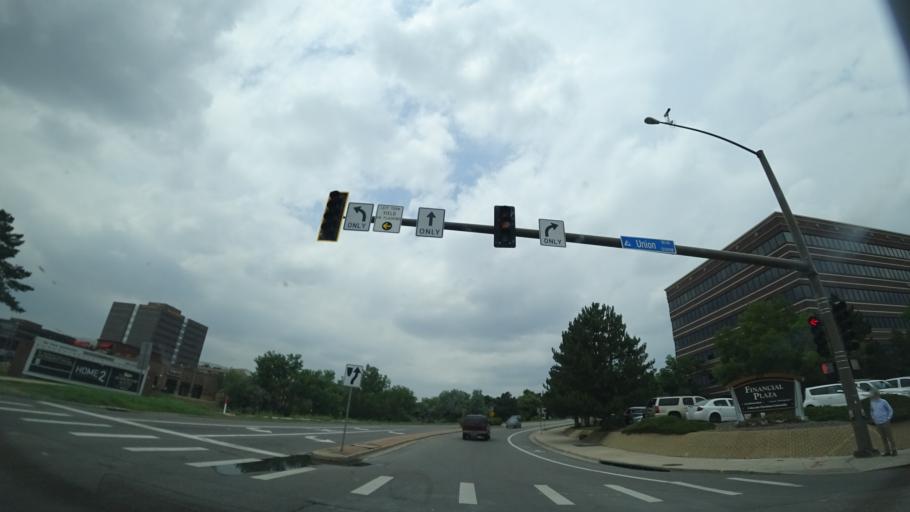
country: US
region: Colorado
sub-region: Jefferson County
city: West Pleasant View
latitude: 39.7181
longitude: -105.1326
